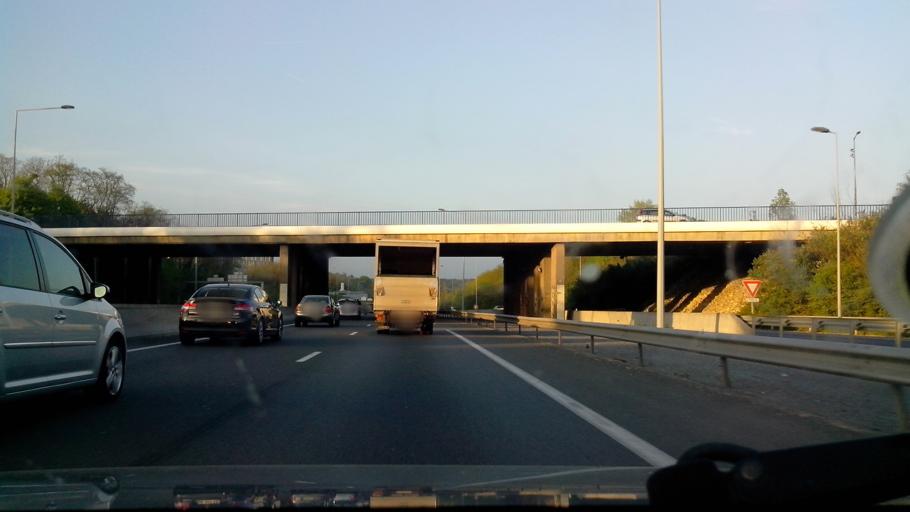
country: FR
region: Ile-de-France
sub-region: Departement de l'Essonne
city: Evry
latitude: 48.6160
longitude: 2.4551
